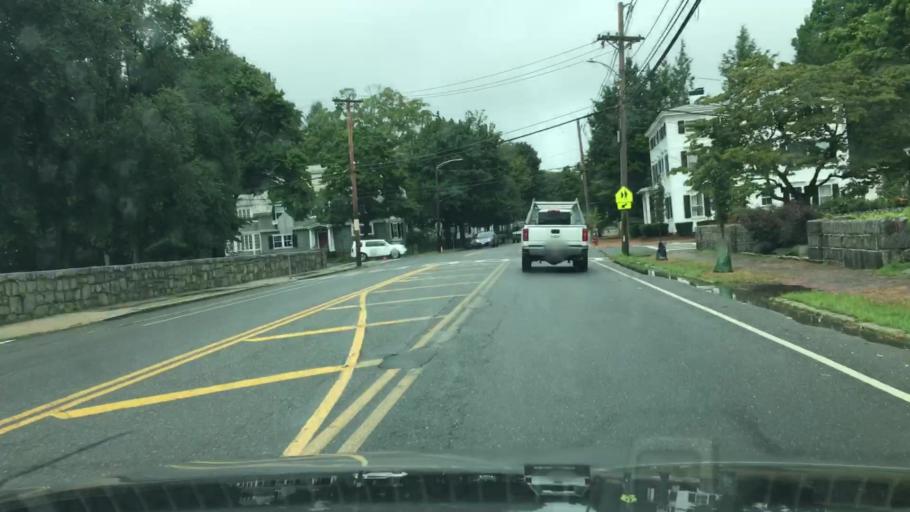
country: US
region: Massachusetts
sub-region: Essex County
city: Newburyport
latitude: 42.8140
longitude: -70.8855
